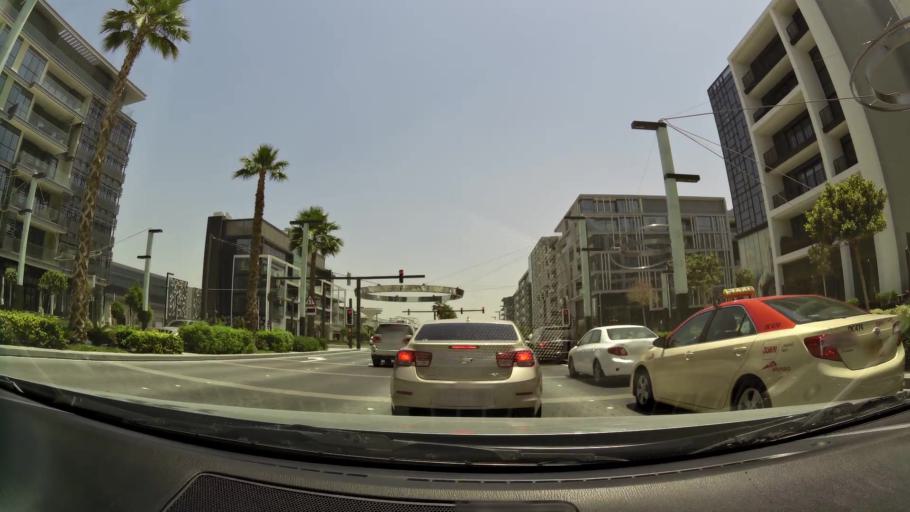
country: AE
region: Dubai
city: Dubai
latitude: 25.2047
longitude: 55.2632
